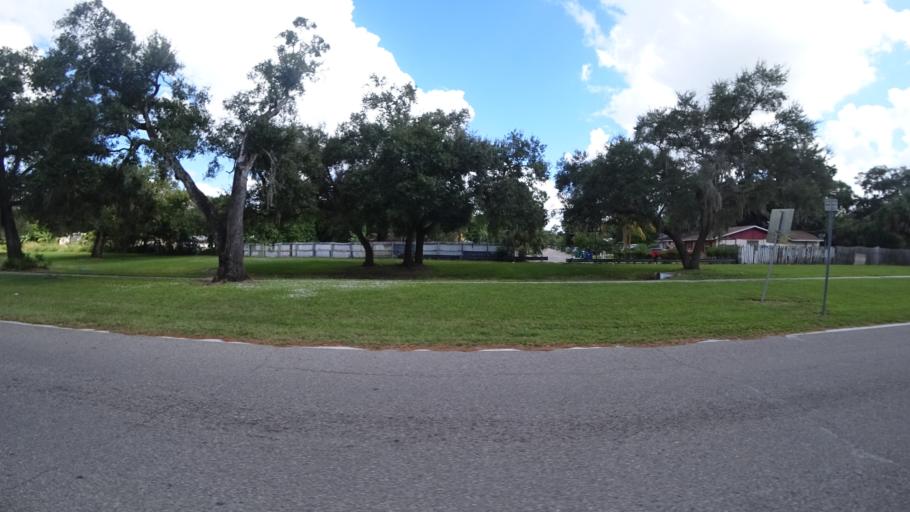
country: US
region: Florida
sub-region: Manatee County
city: Whitfield
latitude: 27.4316
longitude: -82.5551
